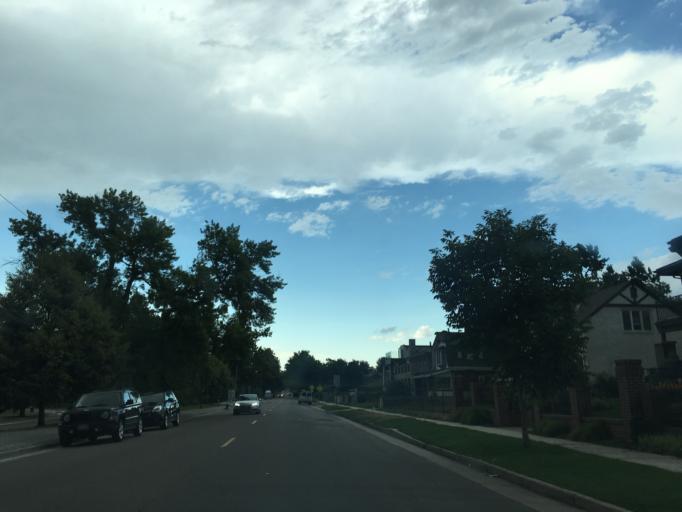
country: US
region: Colorado
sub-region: Arapahoe County
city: Glendale
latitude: 39.7046
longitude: -104.9687
